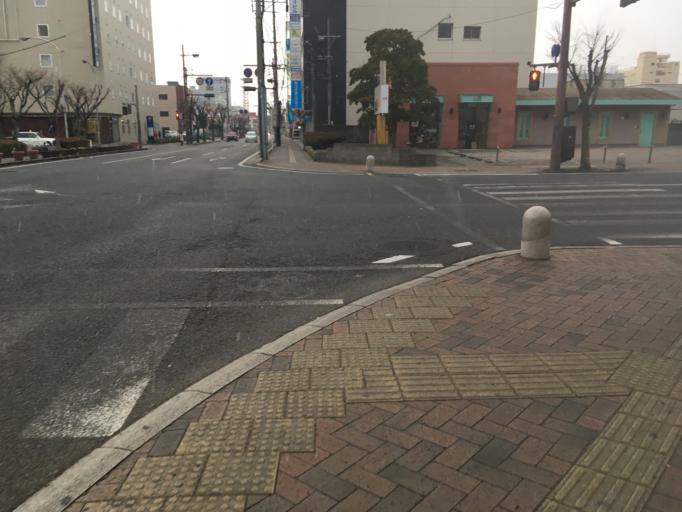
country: JP
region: Saga Prefecture
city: Saga-shi
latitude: 33.2649
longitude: 130.2976
